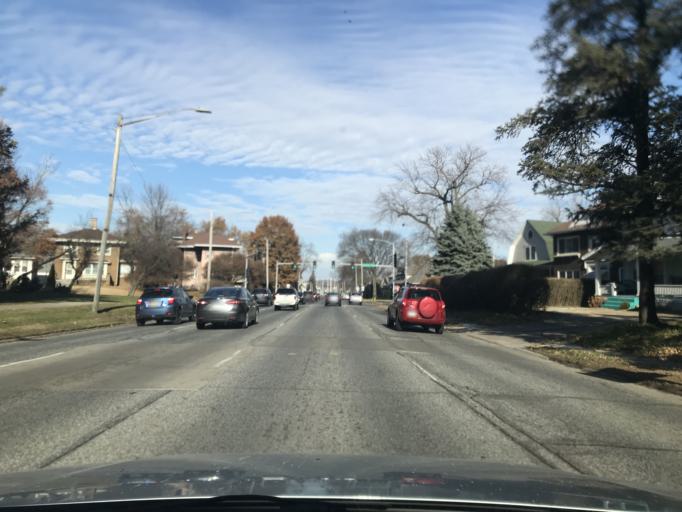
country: US
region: Iowa
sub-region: Scott County
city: Davenport
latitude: 41.5449
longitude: -90.5725
